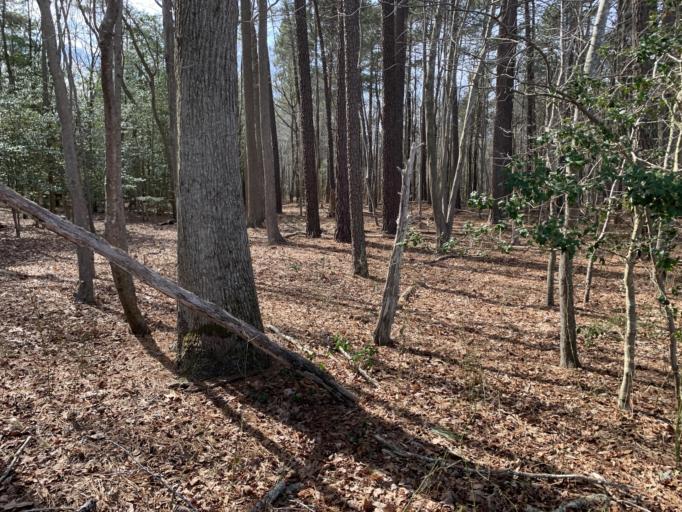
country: US
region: Delaware
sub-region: Sussex County
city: Georgetown
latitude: 38.7469
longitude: -75.3685
